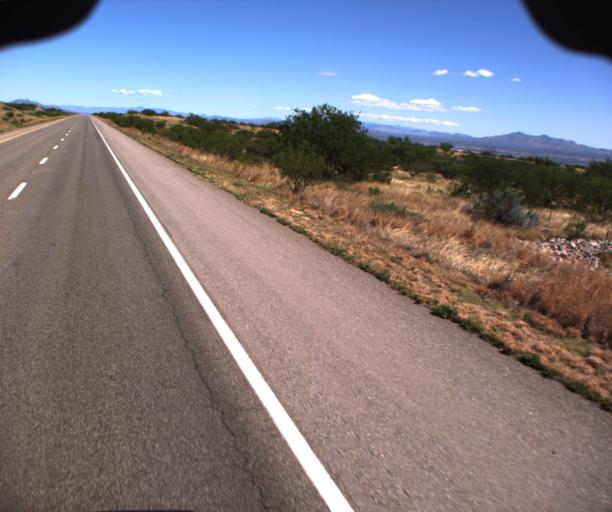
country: US
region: Arizona
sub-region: Cochise County
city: Whetstone
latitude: 31.8699
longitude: -110.3410
